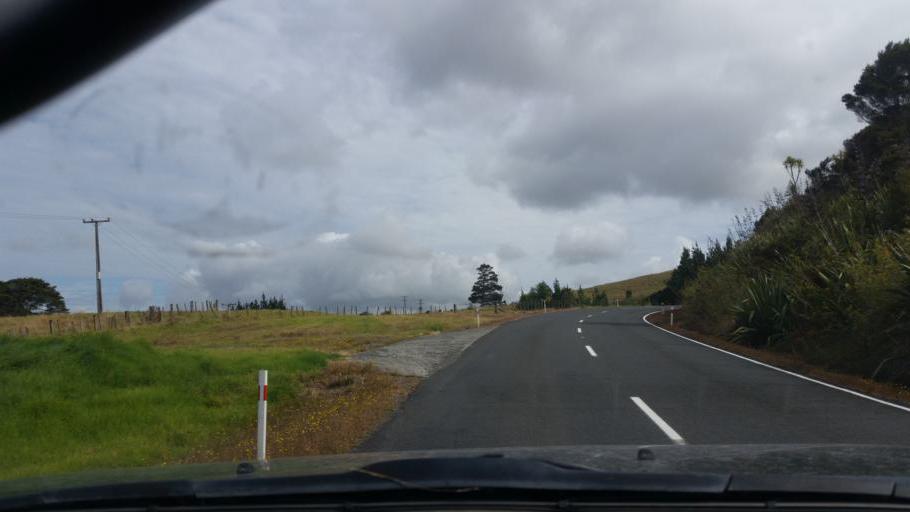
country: NZ
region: Northland
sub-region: Kaipara District
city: Dargaville
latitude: -35.9593
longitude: 173.9249
